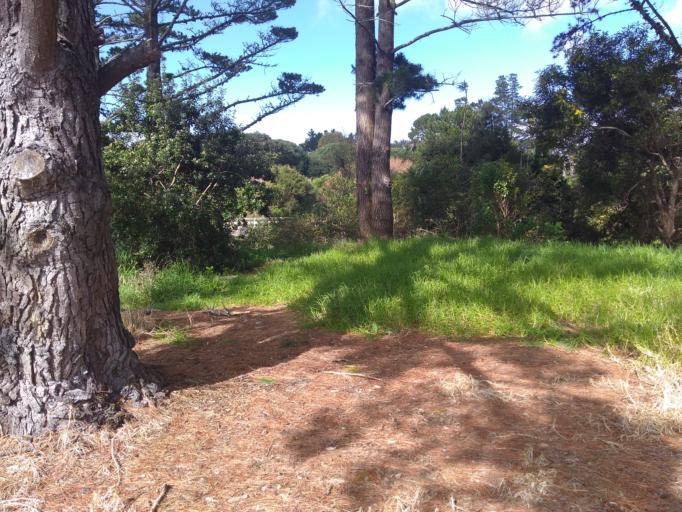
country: NZ
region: Auckland
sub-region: Auckland
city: Rosebank
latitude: -36.8703
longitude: 174.7158
